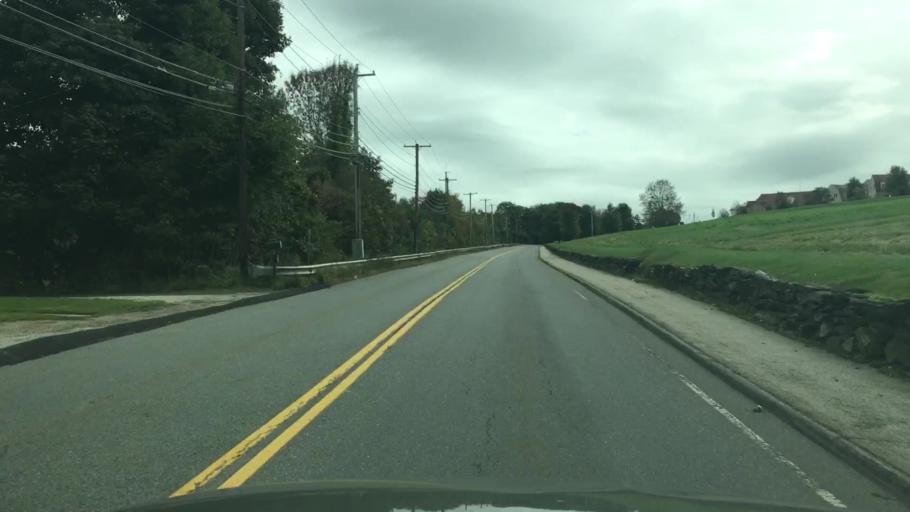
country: US
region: Massachusetts
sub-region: Worcester County
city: Charlton
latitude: 42.1421
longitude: -71.9800
